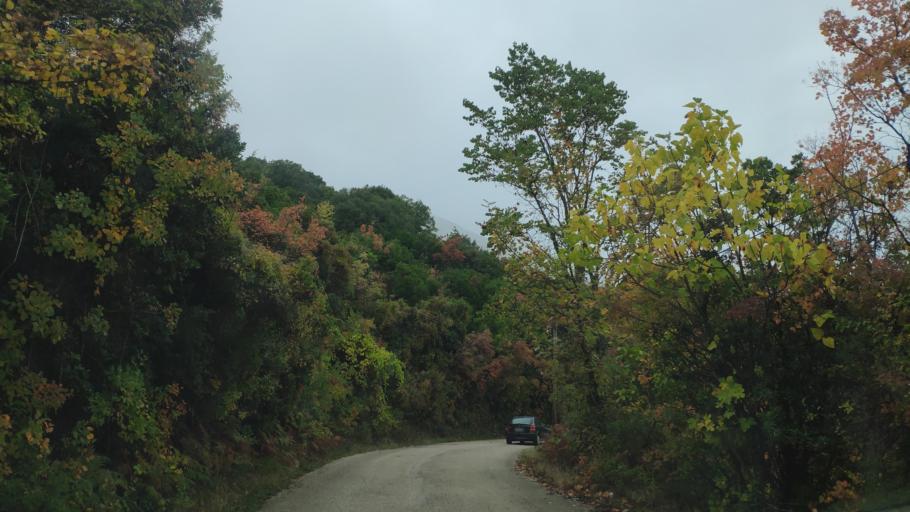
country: GR
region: Epirus
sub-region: Nomos Thesprotias
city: Paramythia
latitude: 39.4697
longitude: 20.6706
